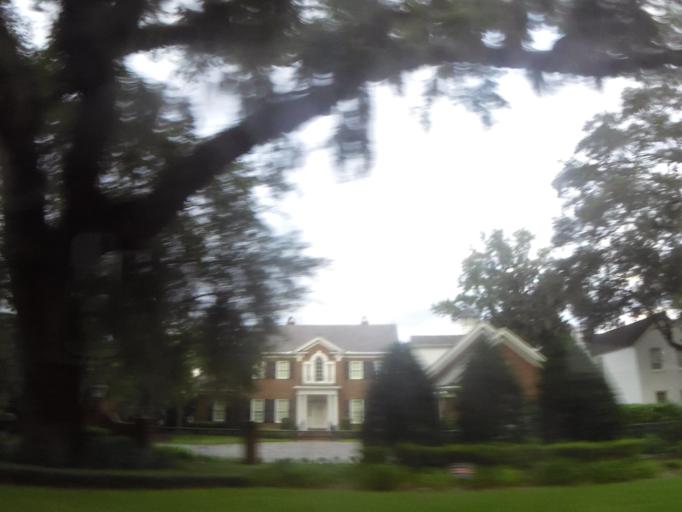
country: US
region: Florida
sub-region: Duval County
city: Jacksonville
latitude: 30.2670
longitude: -81.7010
